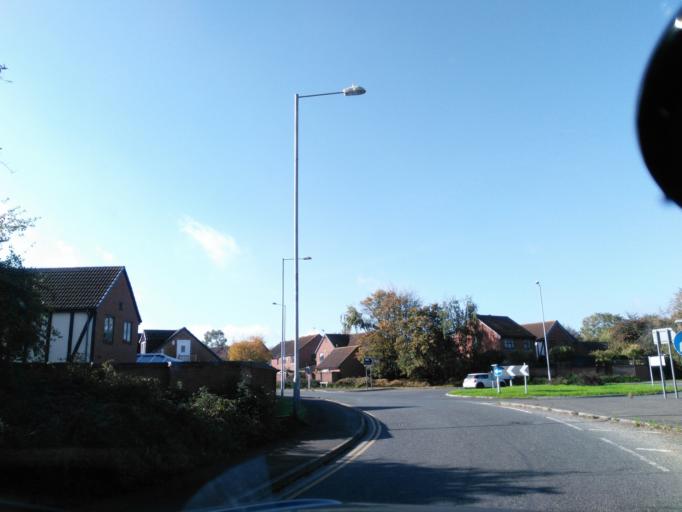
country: GB
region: England
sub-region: Wiltshire
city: Melksham
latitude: 51.3604
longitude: -2.1201
